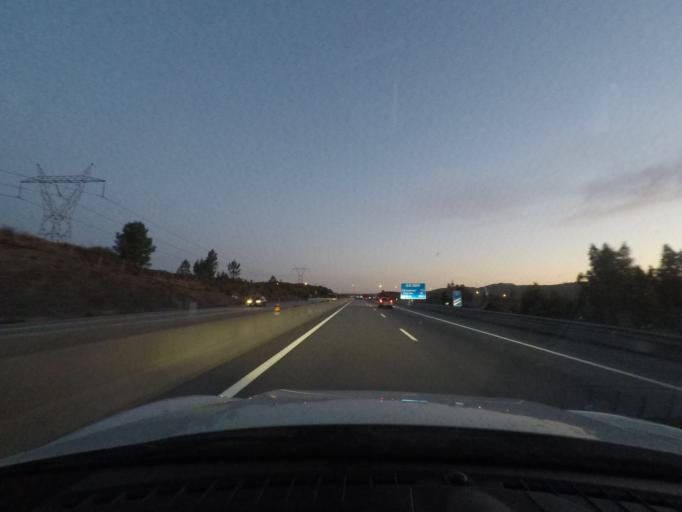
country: PT
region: Porto
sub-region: Valongo
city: Campo
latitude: 41.1732
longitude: -8.4487
